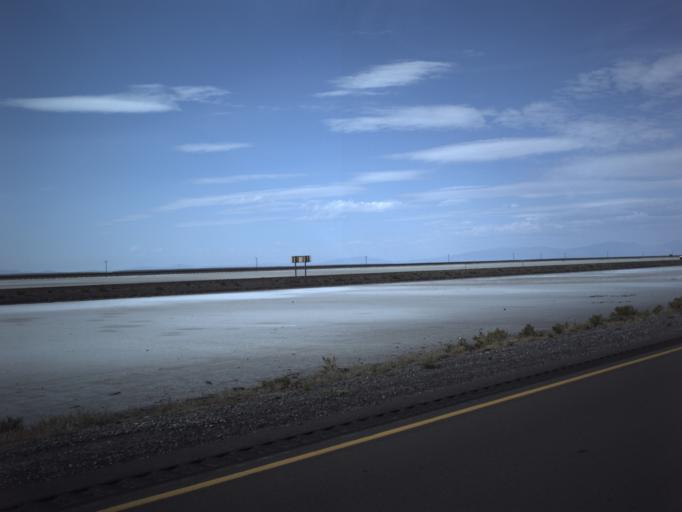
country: US
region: Utah
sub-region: Tooele County
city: Wendover
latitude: 40.7307
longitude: -113.4509
